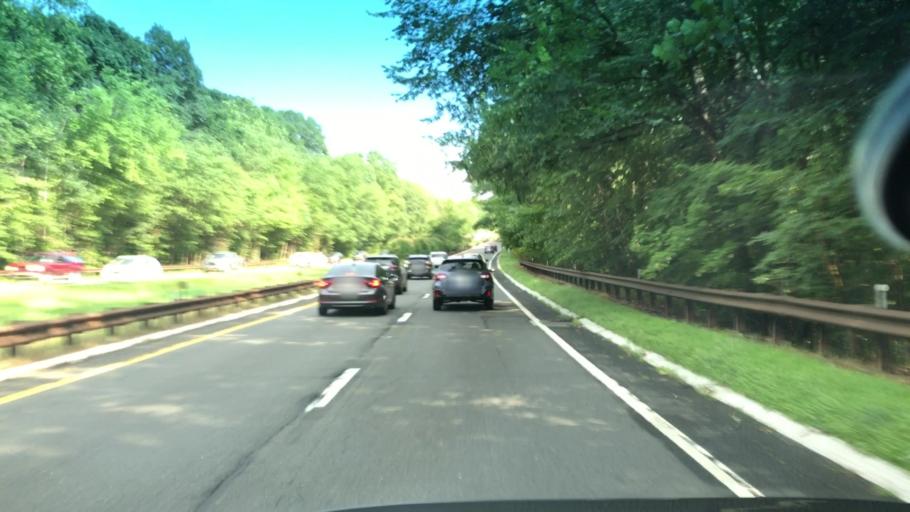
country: US
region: New York
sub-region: Rockland County
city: Blauvelt
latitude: 41.0570
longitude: -73.9679
